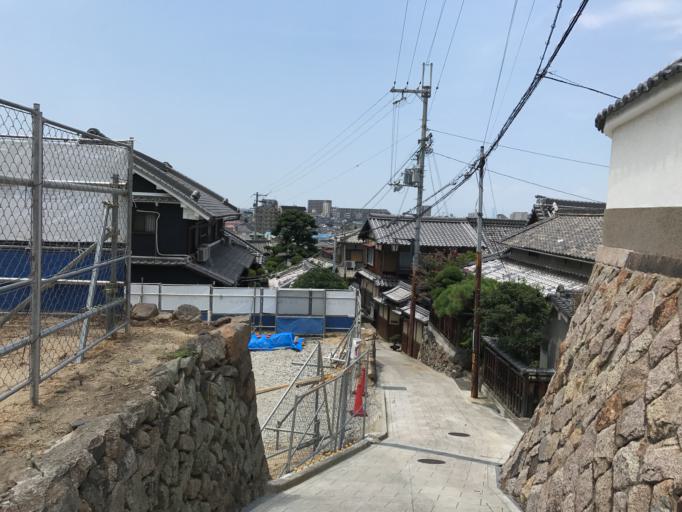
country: JP
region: Osaka
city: Kashihara
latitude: 34.5833
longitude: 135.6346
